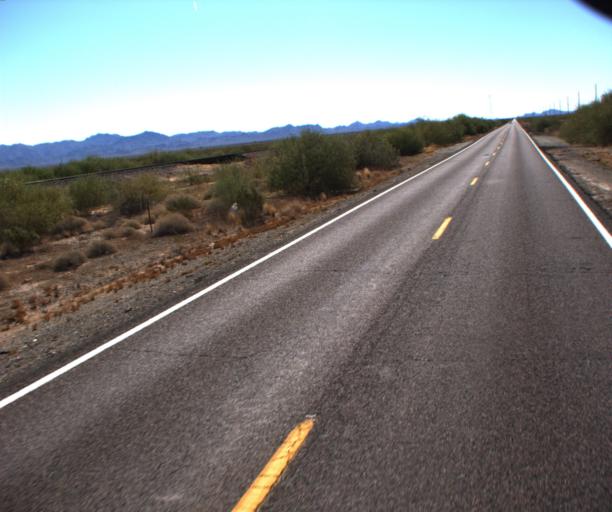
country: US
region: Arizona
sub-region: La Paz County
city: Salome
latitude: 33.8491
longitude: -113.9017
